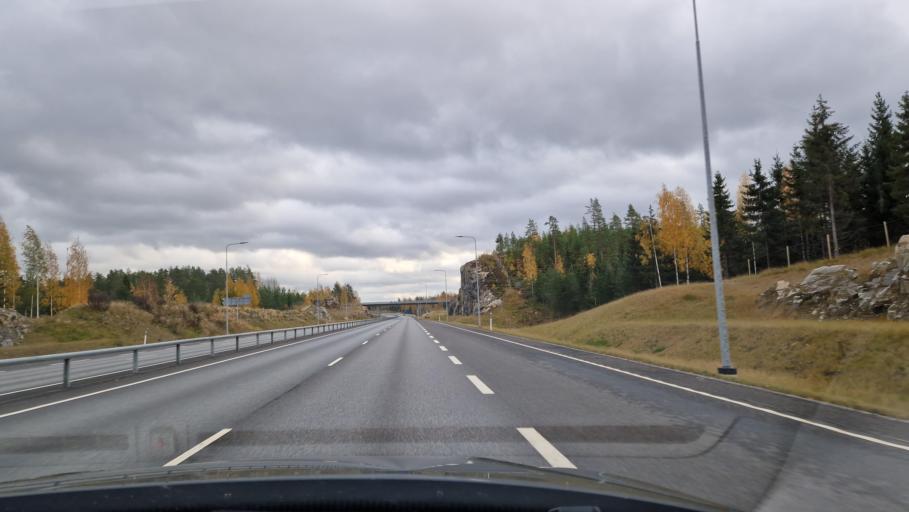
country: FI
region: Southern Savonia
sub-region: Mikkeli
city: Mikkeli
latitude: 61.7552
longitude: 27.5441
